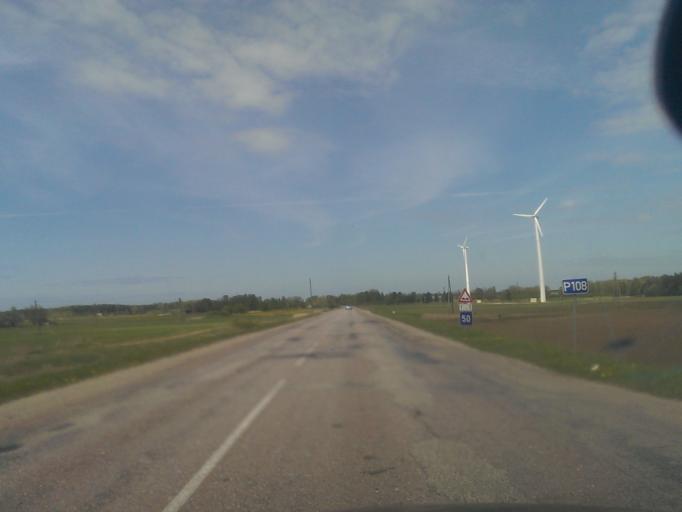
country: LV
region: Ventspils Rajons
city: Piltene
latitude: 57.2648
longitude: 21.5858
